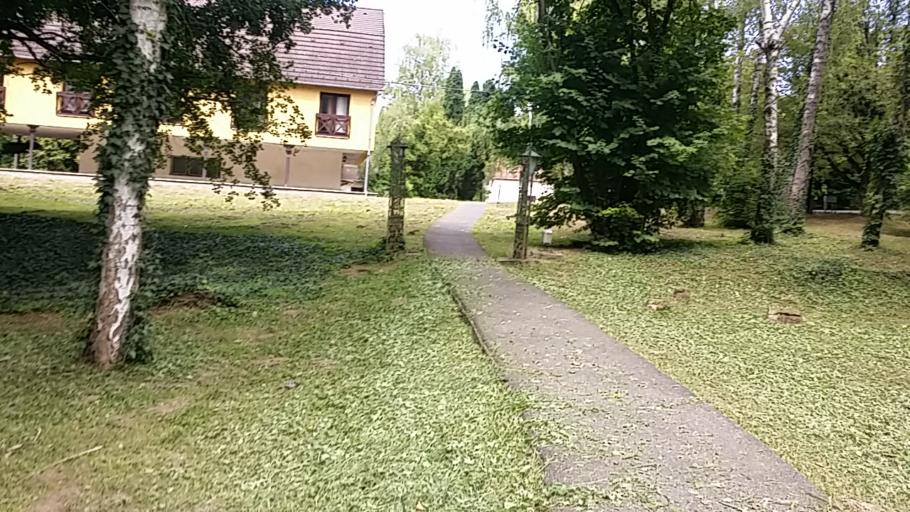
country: HU
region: Somogy
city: Taszar
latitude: 46.3561
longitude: 17.9946
